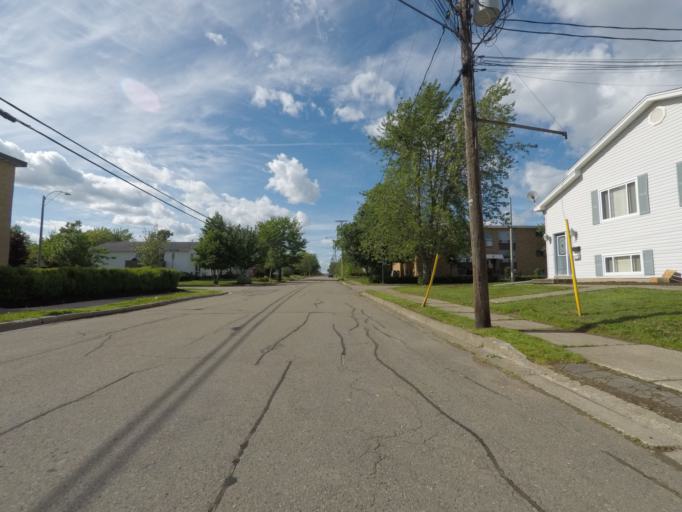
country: CA
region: New Brunswick
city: Moncton
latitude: 46.0981
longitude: -64.8199
